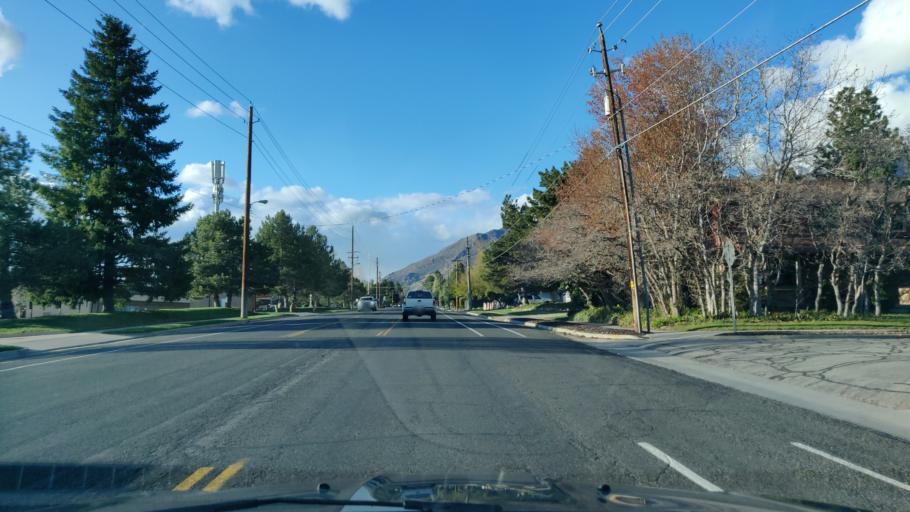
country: US
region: Utah
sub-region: Salt Lake County
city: Cottonwood Heights
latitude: 40.6071
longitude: -111.7959
